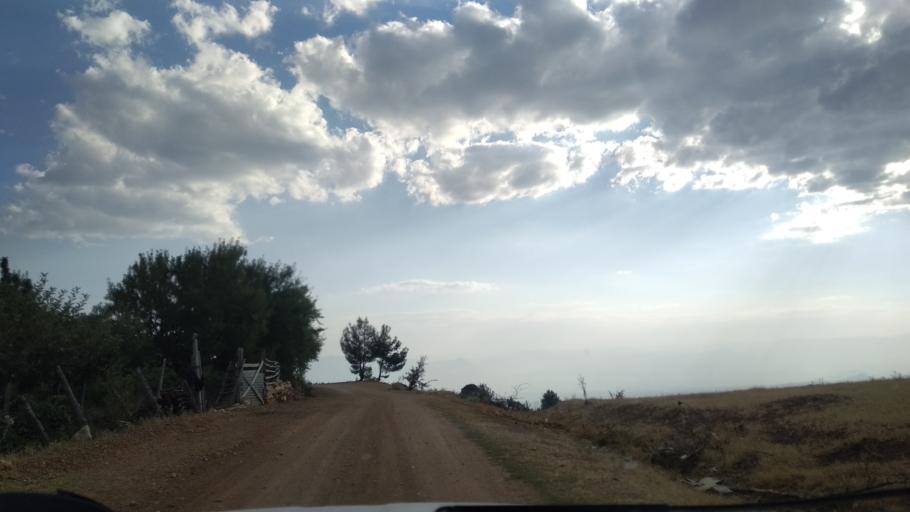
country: TR
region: Mersin
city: Sarikavak
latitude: 36.5924
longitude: 33.6796
